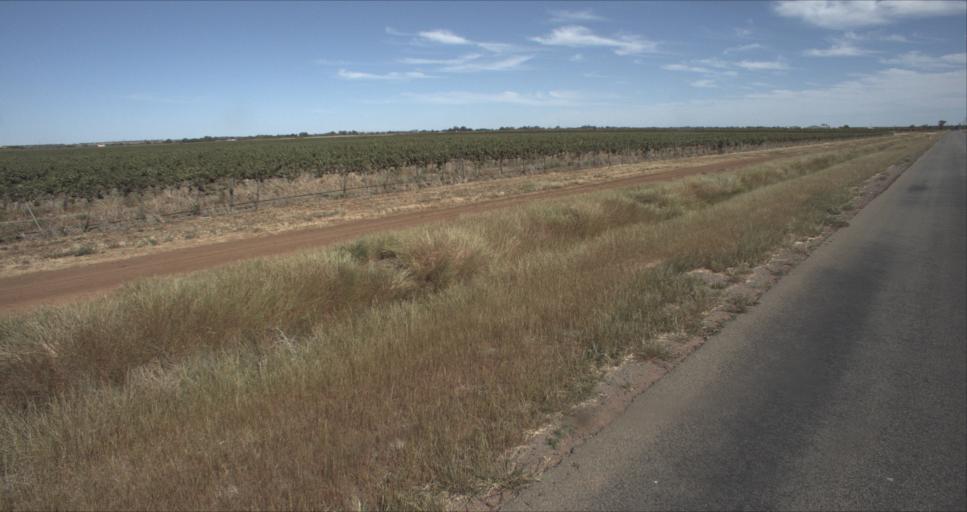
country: AU
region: New South Wales
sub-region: Leeton
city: Leeton
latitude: -34.5789
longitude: 146.3802
